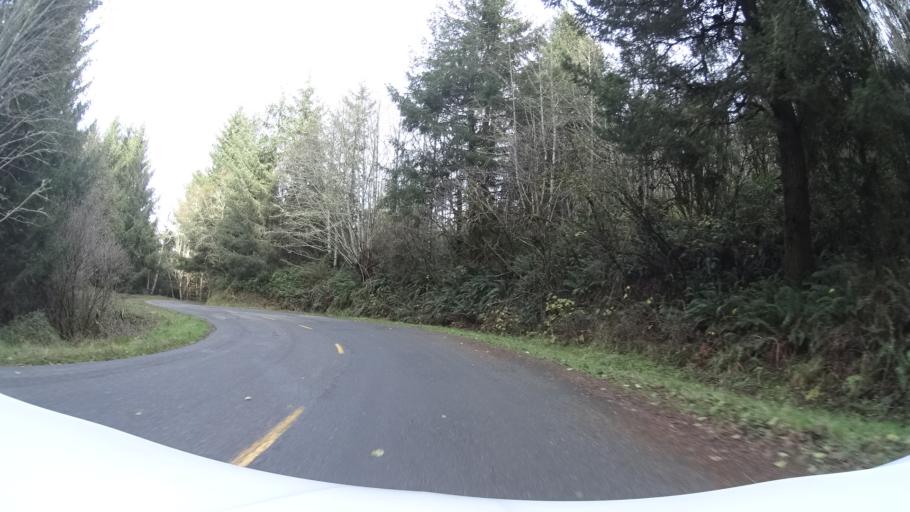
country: US
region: California
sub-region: Humboldt County
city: Ferndale
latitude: 40.5419
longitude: -124.2788
